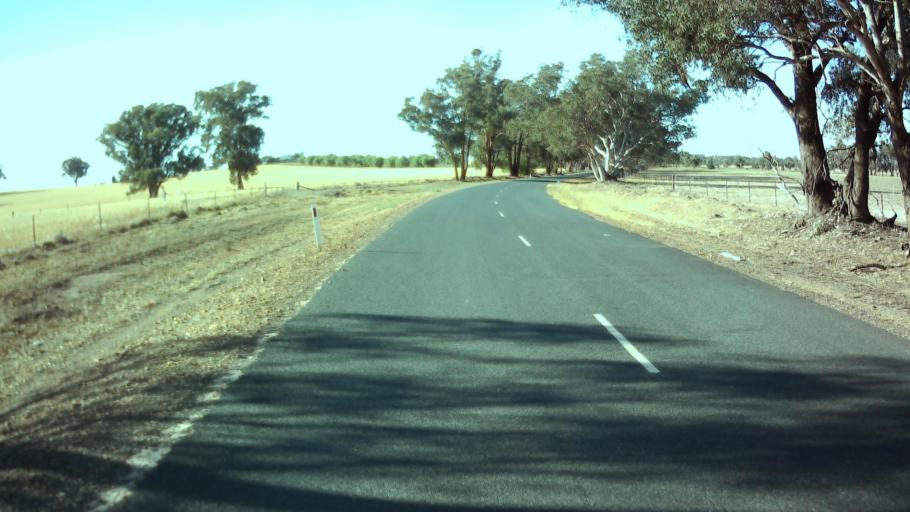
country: AU
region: New South Wales
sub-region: Weddin
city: Grenfell
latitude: -33.9761
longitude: 148.1412
